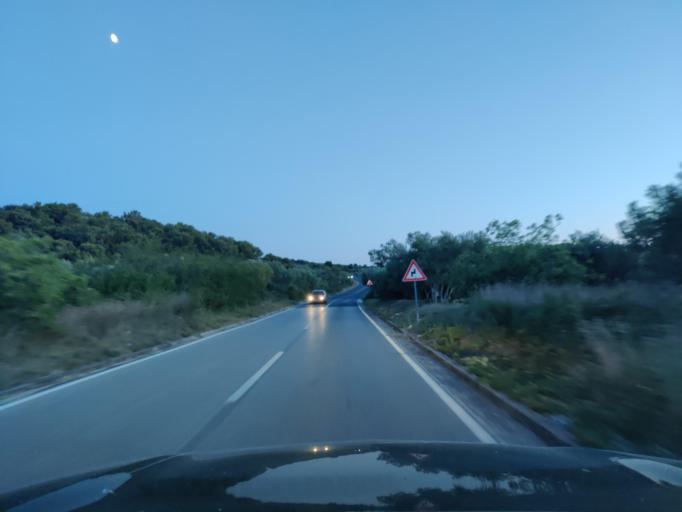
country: HR
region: Sibensko-Kniniska
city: Murter
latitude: 43.8185
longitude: 15.6010
